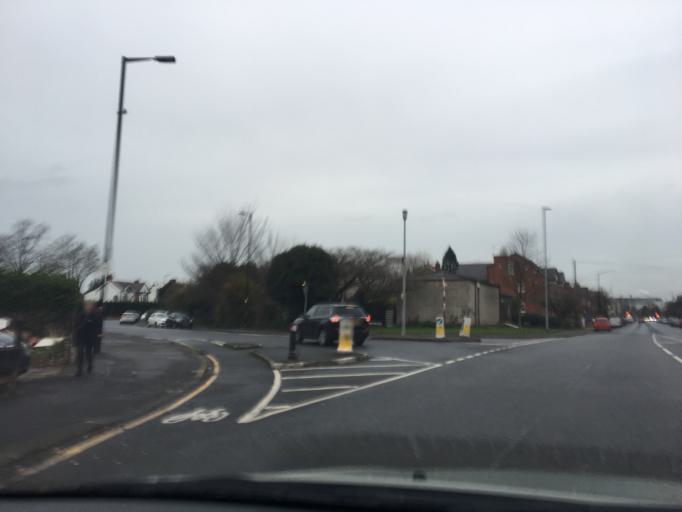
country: GB
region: England
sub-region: Trafford
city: Stretford
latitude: 53.4473
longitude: -2.3142
